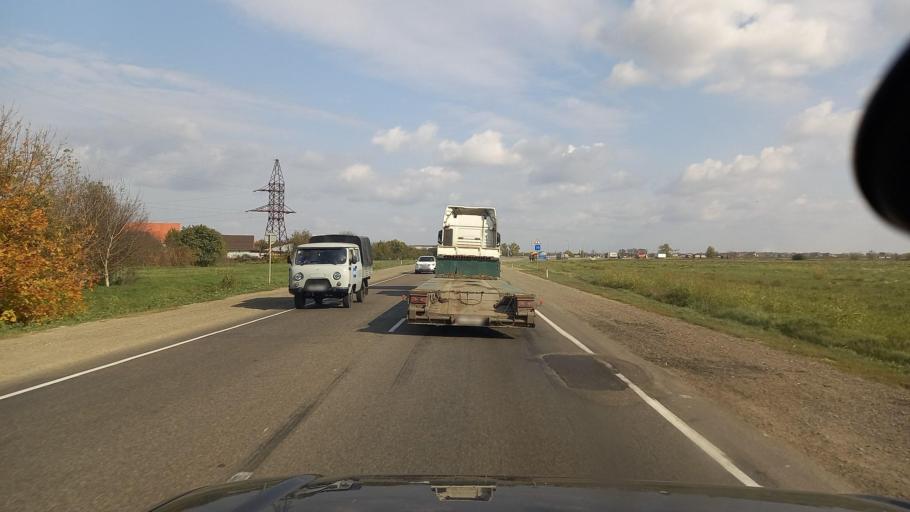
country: RU
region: Krasnodarskiy
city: Abinsk
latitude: 44.8554
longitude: 38.1873
